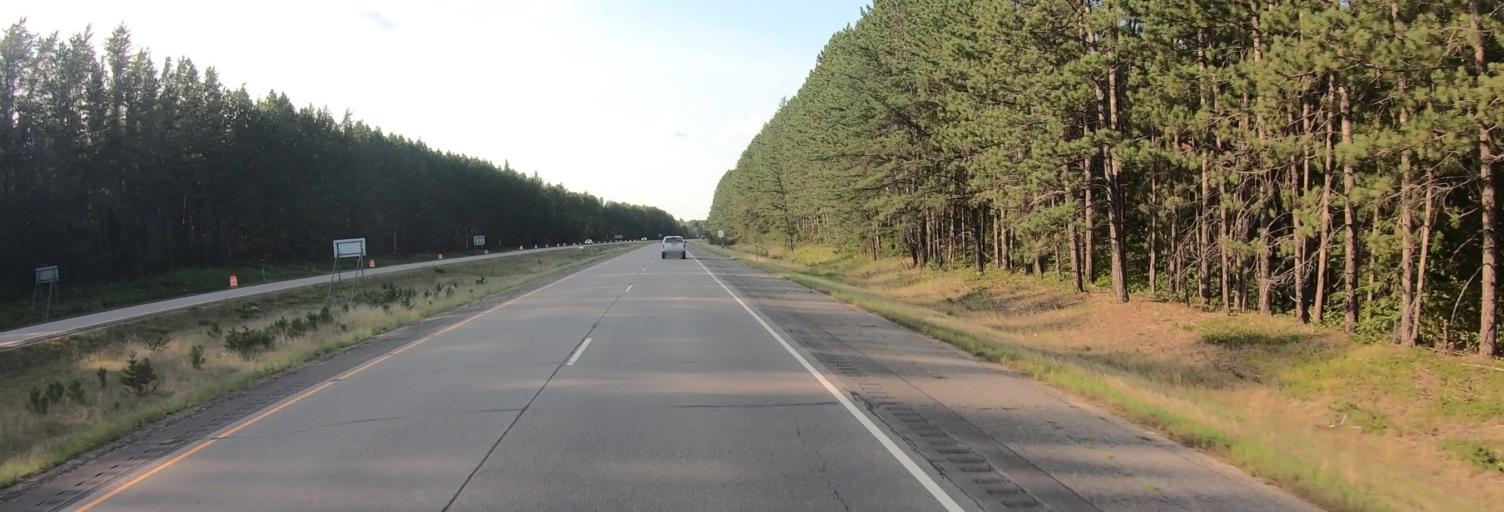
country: US
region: Minnesota
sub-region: Saint Louis County
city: Eveleth
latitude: 47.4031
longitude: -92.5191
